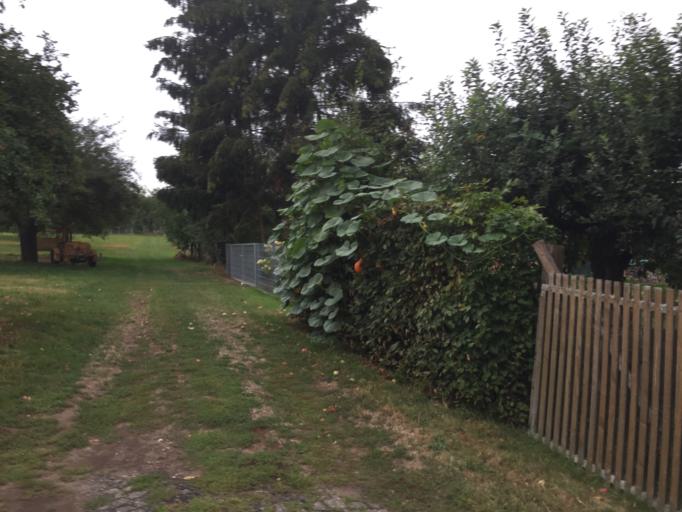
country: DE
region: Hesse
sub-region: Regierungsbezirk Giessen
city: Grossen Buseck
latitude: 50.5759
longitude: 8.7540
